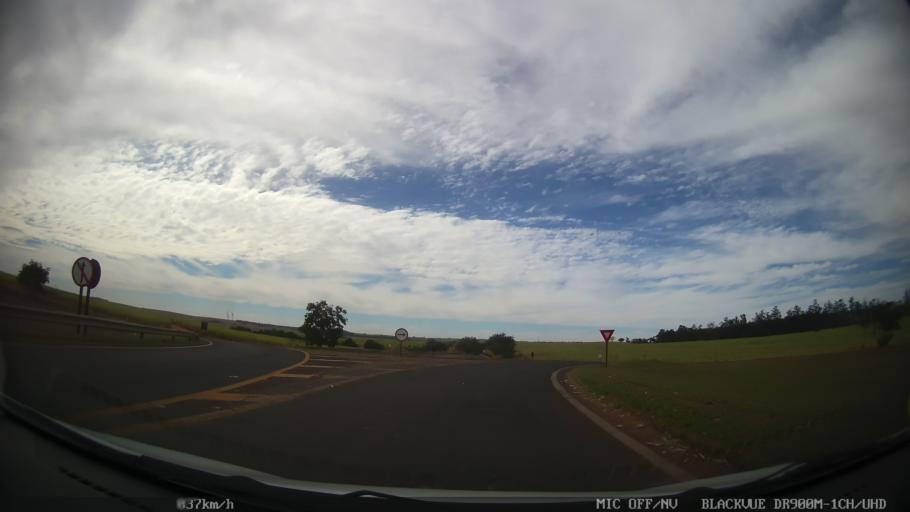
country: BR
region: Sao Paulo
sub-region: Santa Adelia
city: Santa Adelia
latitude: -21.2764
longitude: -48.8601
